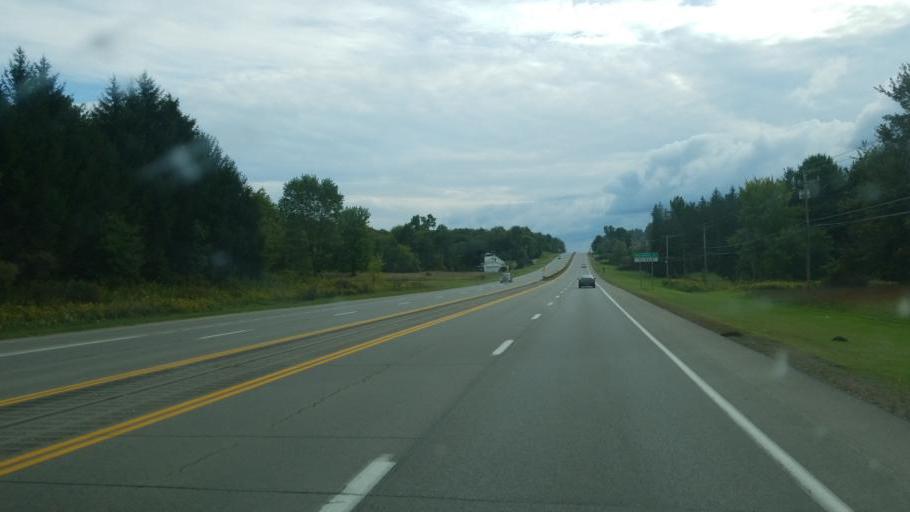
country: US
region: Pennsylvania
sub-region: Mercer County
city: Sharpsville
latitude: 41.2774
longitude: -80.4365
